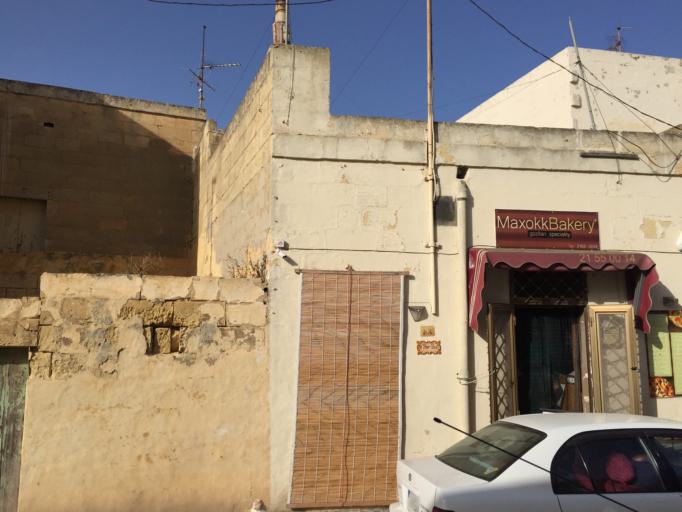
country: MT
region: In-Nadur
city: Nadur
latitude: 36.0389
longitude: 14.2977
